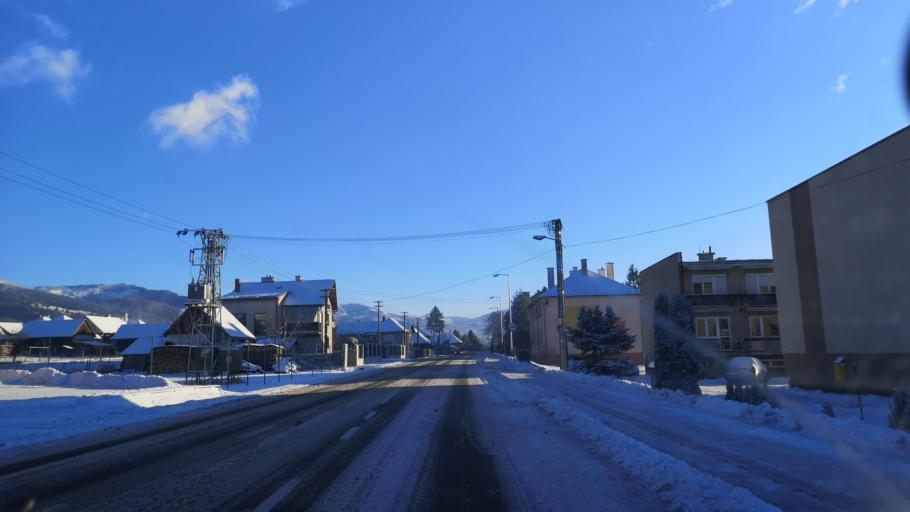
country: SK
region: Zilinsky
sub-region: Okres Liptovsky Mikulas
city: Hybe
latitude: 48.8511
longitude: 19.8480
